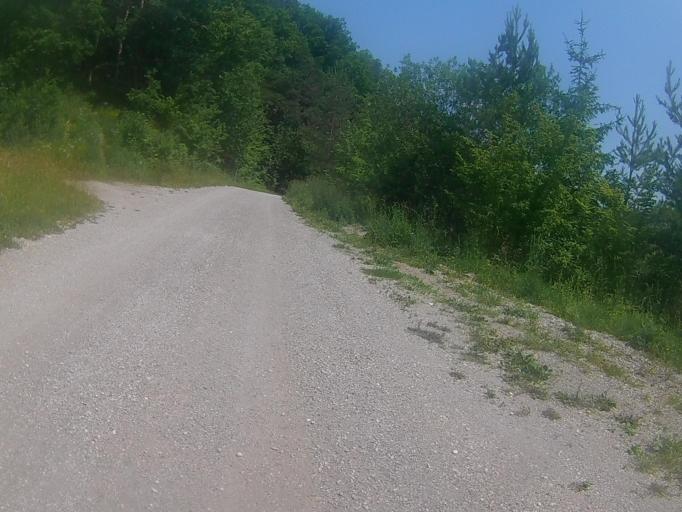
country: SI
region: Maribor
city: Bresternica
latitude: 46.5945
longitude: 15.5873
